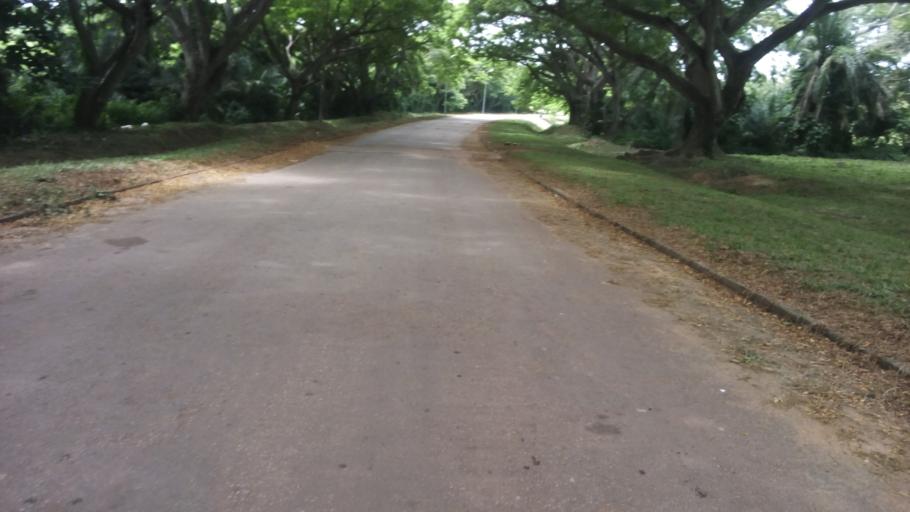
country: GH
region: Central
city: Cape Coast
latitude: 5.1264
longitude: -1.2893
